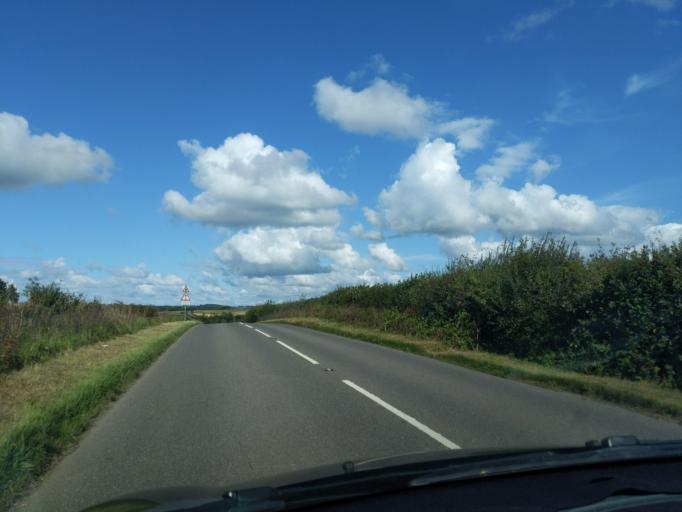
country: GB
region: England
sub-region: Cornwall
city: Werrington
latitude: 50.6658
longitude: -4.3293
